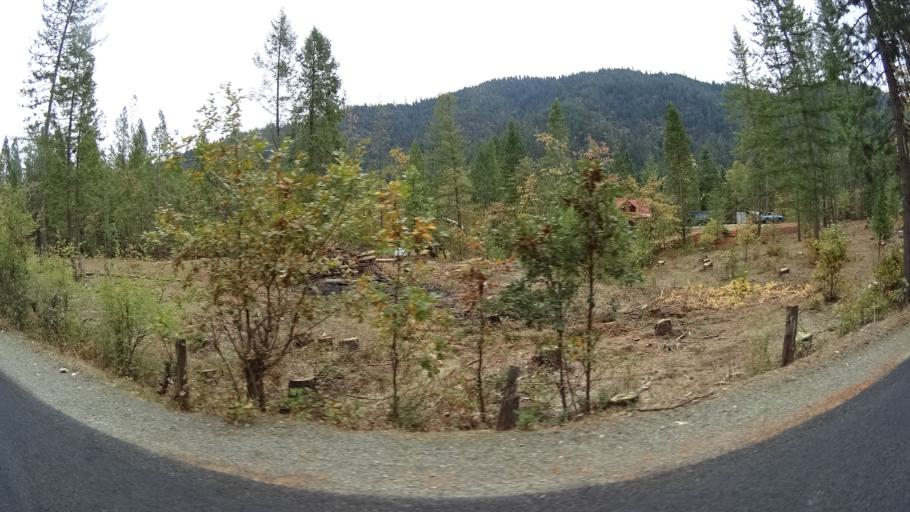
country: US
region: California
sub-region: Siskiyou County
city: Happy Camp
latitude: 41.8558
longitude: -123.1701
